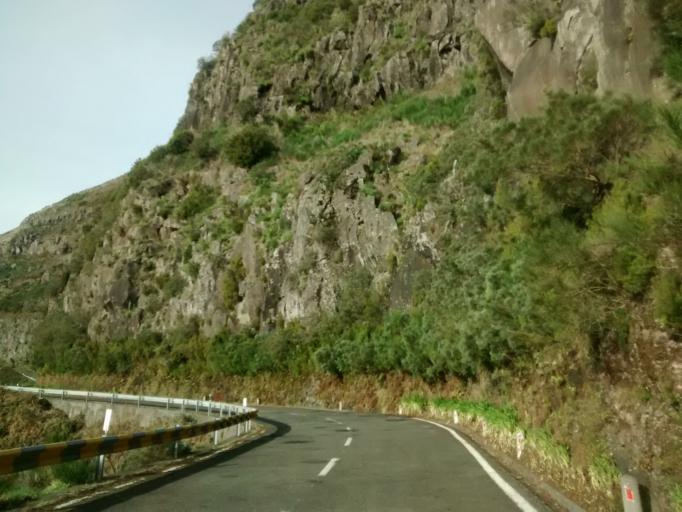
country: PT
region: Madeira
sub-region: Sao Vicente
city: Sao Vicente
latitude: 32.7369
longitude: -17.0504
